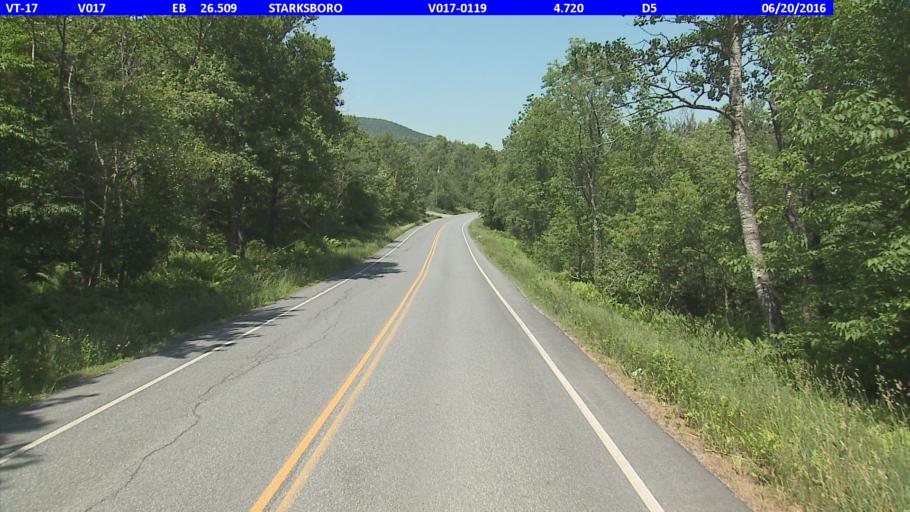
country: US
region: Vermont
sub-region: Addison County
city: Bristol
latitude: 44.2071
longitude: -72.9652
